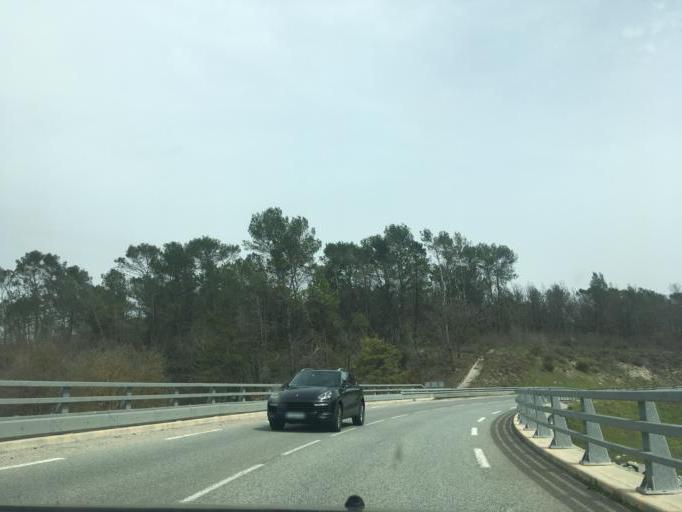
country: FR
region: Provence-Alpes-Cote d'Azur
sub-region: Departement du Var
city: Callian
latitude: 43.6000
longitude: 6.7382
